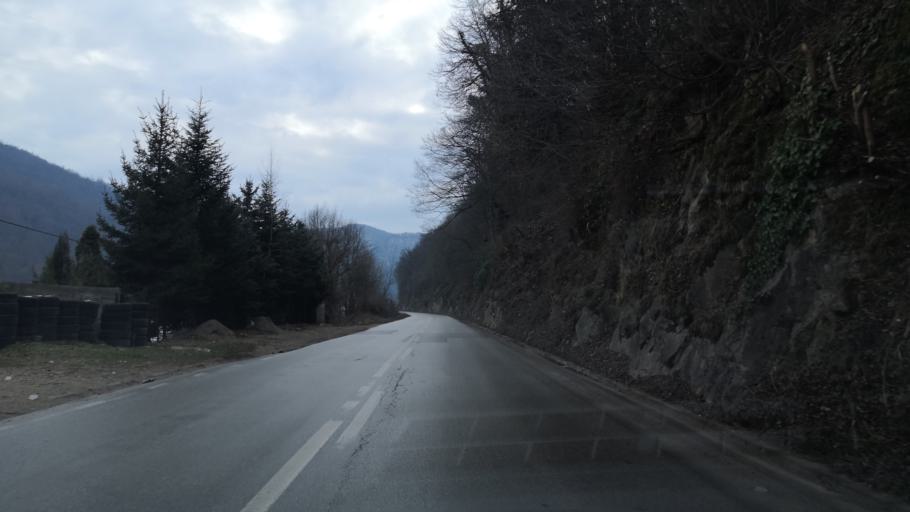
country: RS
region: Central Serbia
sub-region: Macvanski Okrug
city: Mali Zvornik
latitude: 44.3524
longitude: 19.1080
